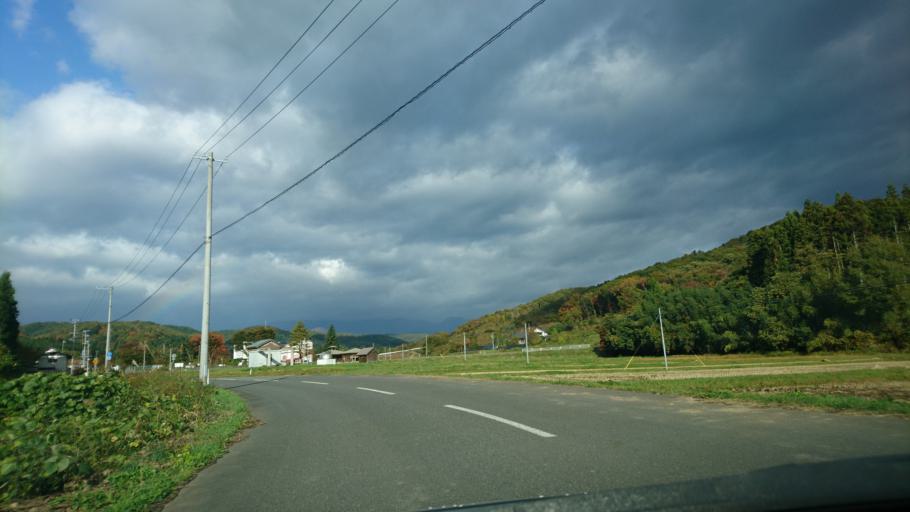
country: JP
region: Iwate
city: Mizusawa
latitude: 39.0858
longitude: 140.9898
